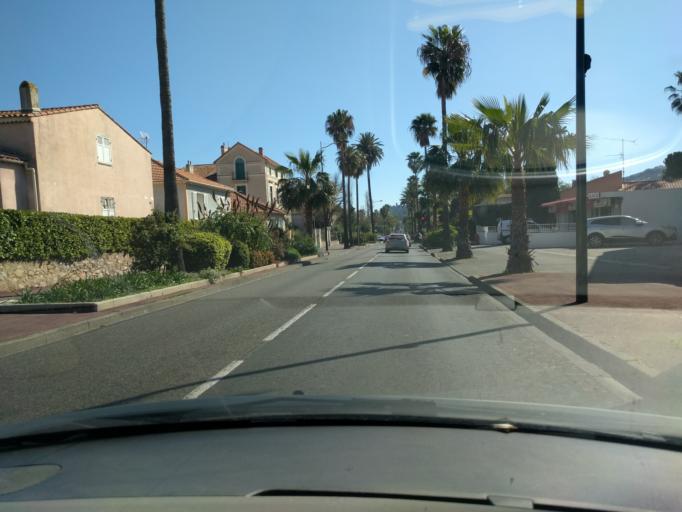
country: FR
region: Provence-Alpes-Cote d'Azur
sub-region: Departement du Var
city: Hyeres
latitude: 43.1161
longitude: 6.1228
